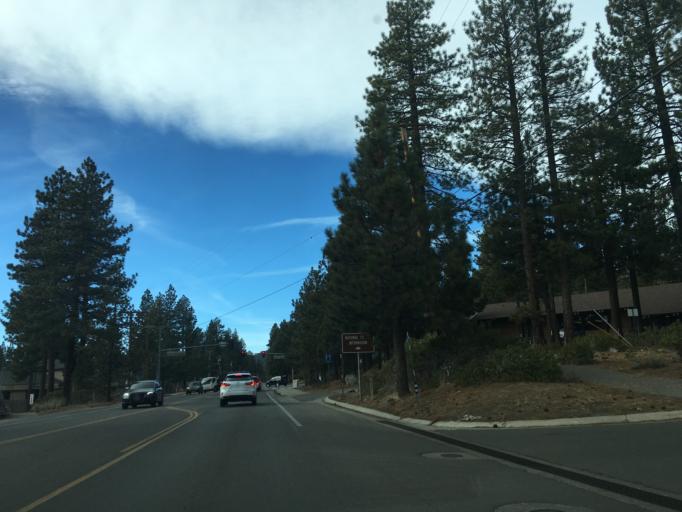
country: US
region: Nevada
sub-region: Washoe County
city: Incline Village
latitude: 39.2497
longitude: -119.9513
